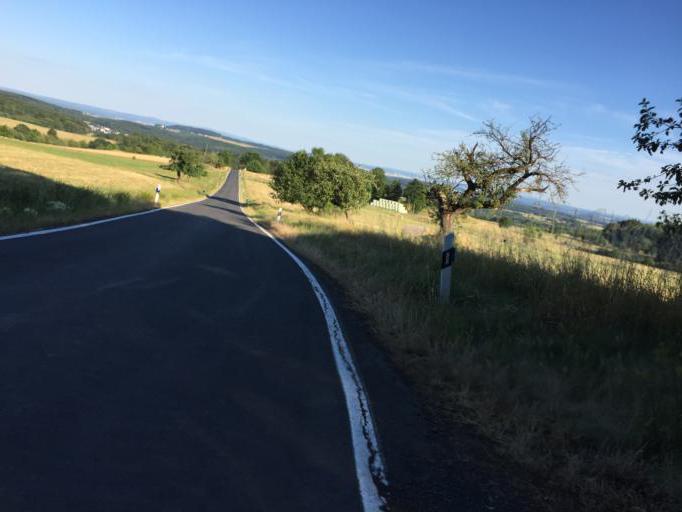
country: DE
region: Rheinland-Pfalz
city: Ettinghausen
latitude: 50.5162
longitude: 7.8906
